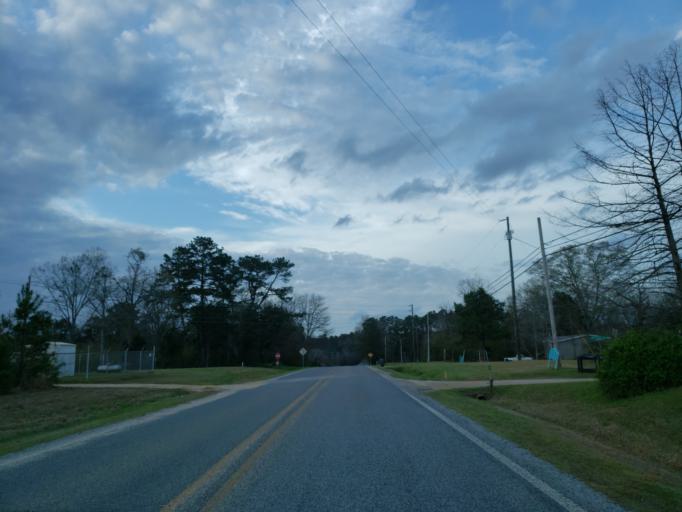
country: US
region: Mississippi
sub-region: Clarke County
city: Stonewall
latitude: 32.2175
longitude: -88.6989
